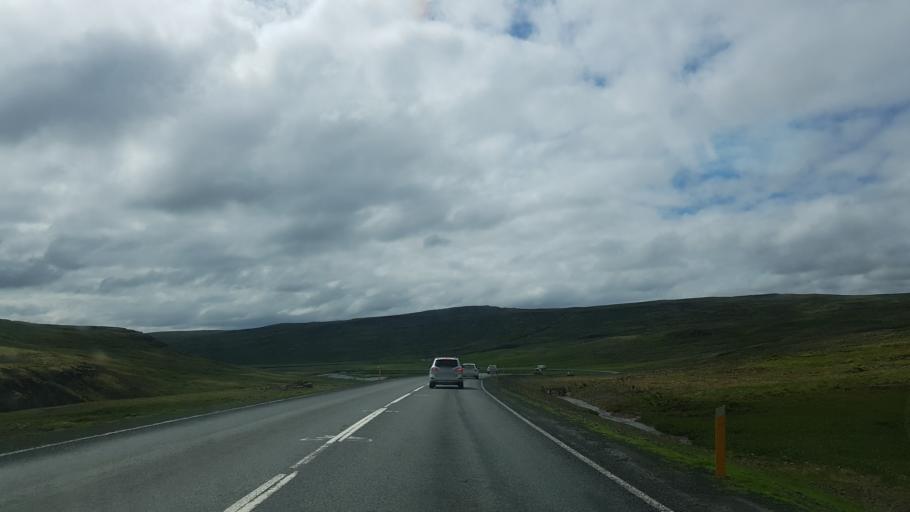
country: IS
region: West
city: Borgarnes
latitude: 64.9088
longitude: -21.1640
